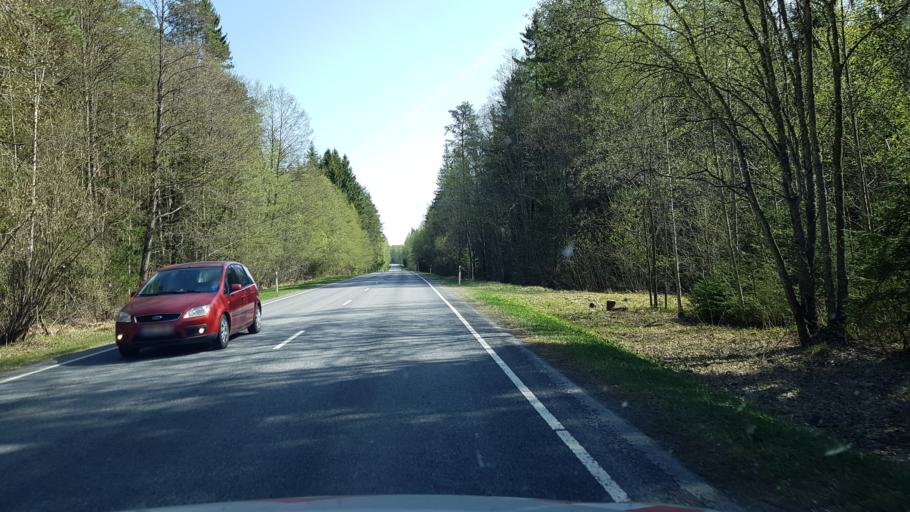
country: EE
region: Viljandimaa
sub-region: Moisakuela linn
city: Moisakula
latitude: 58.2582
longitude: 25.2237
